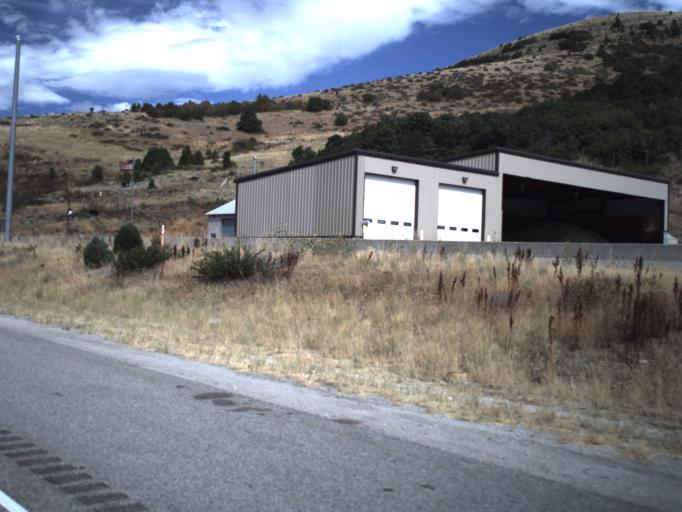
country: US
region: Utah
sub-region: Box Elder County
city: Brigham City
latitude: 41.5496
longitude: -111.9537
